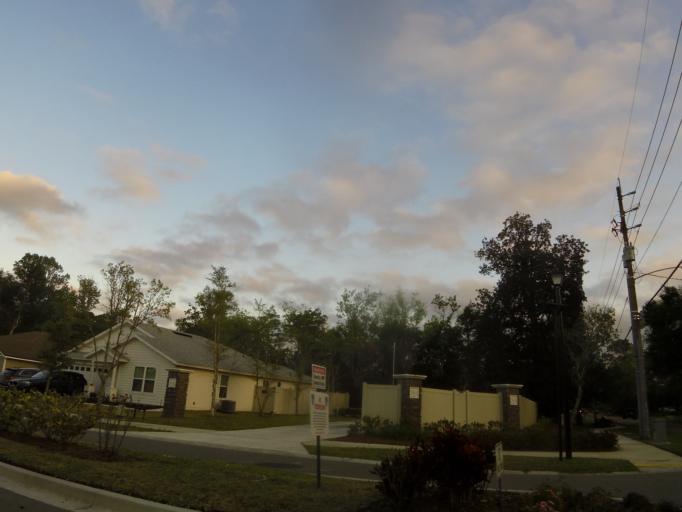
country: US
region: Florida
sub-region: Duval County
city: Jacksonville
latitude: 30.4702
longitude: -81.6260
